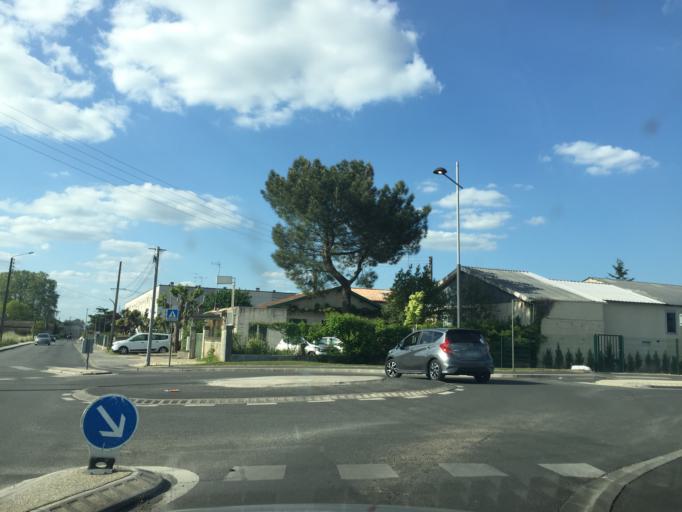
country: FR
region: Aquitaine
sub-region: Departement de la Gironde
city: Libourne
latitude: 44.9319
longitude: -0.2410
